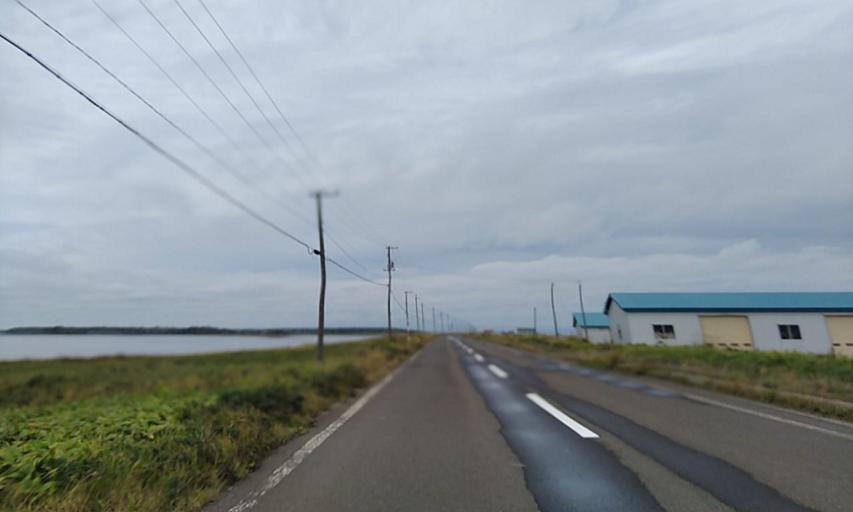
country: JP
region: Hokkaido
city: Shibetsu
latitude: 43.5983
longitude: 145.3173
